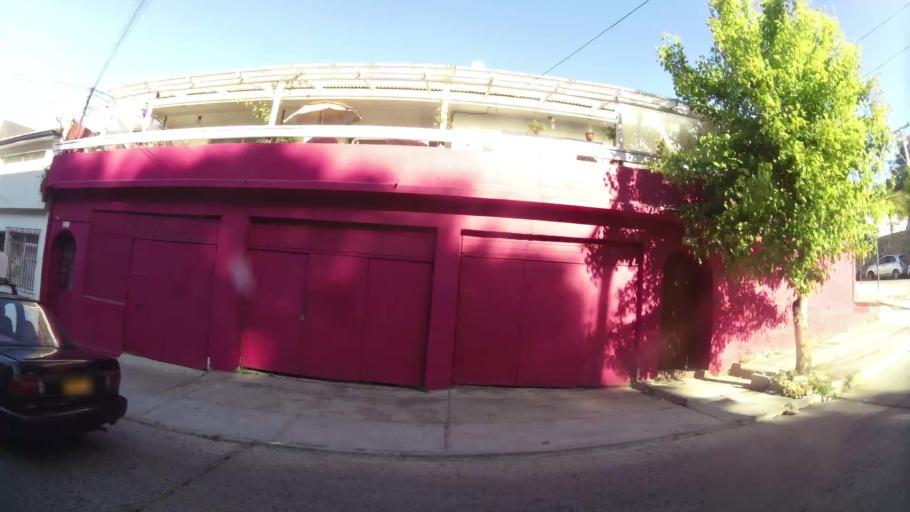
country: CL
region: Valparaiso
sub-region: Provincia de Valparaiso
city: Vina del Mar
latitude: -33.0319
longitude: -71.5631
